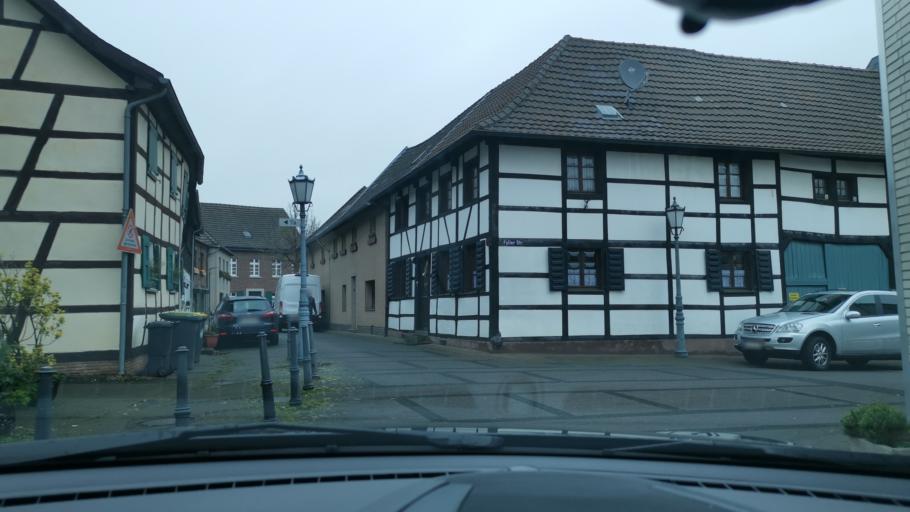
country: DE
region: North Rhine-Westphalia
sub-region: Regierungsbezirk Dusseldorf
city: Juchen
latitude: 51.1030
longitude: 6.5018
